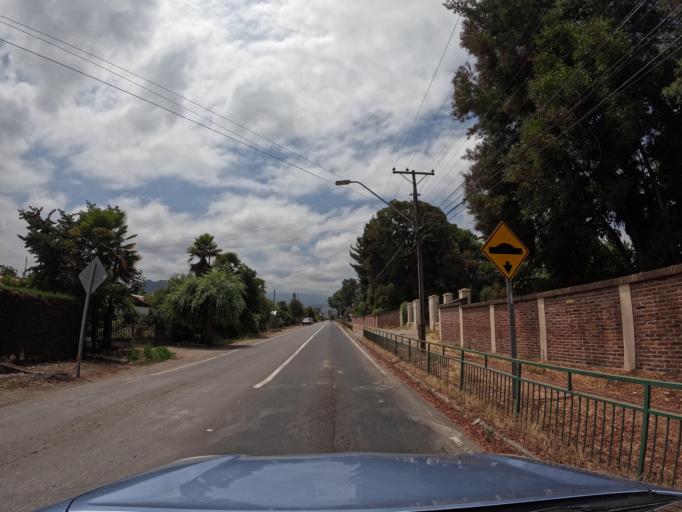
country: CL
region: O'Higgins
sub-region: Provincia de Colchagua
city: Chimbarongo
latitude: -34.7346
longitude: -70.9788
